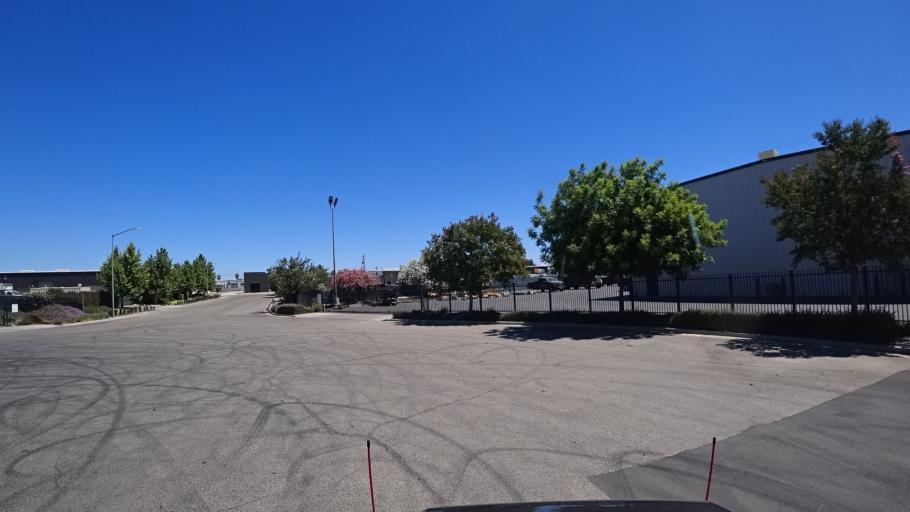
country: US
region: California
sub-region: Fresno County
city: Fresno
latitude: 36.7029
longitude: -119.7760
